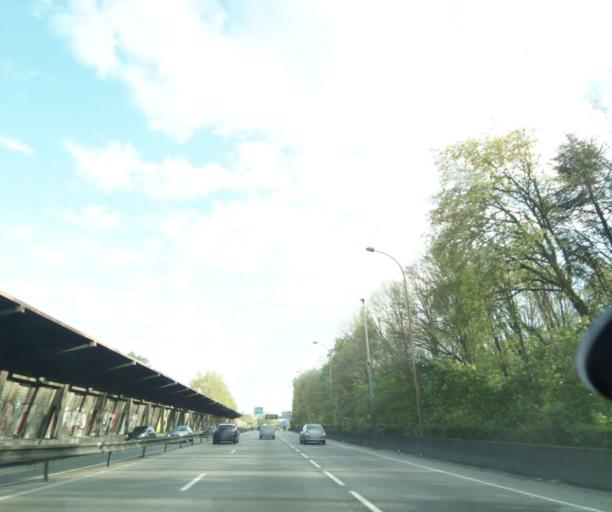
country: FR
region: Ile-de-France
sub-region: Departement des Hauts-de-Seine
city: Meudon
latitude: 48.7899
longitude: 2.2208
